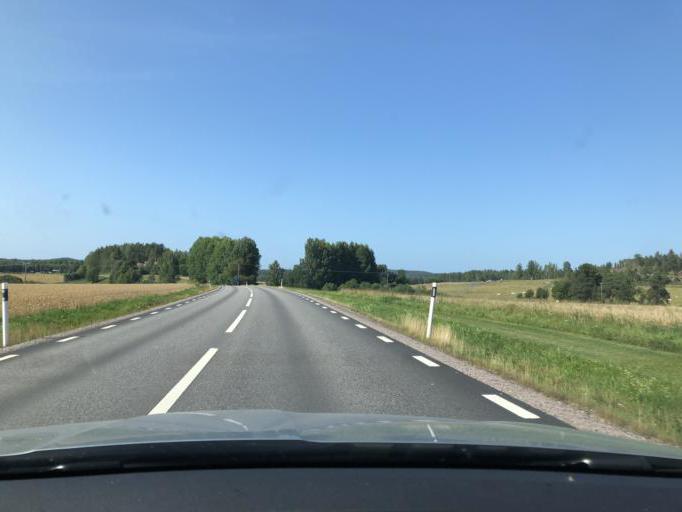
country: SE
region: Dalarna
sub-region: Saters Kommun
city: Saeter
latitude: 60.4041
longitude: 15.8726
